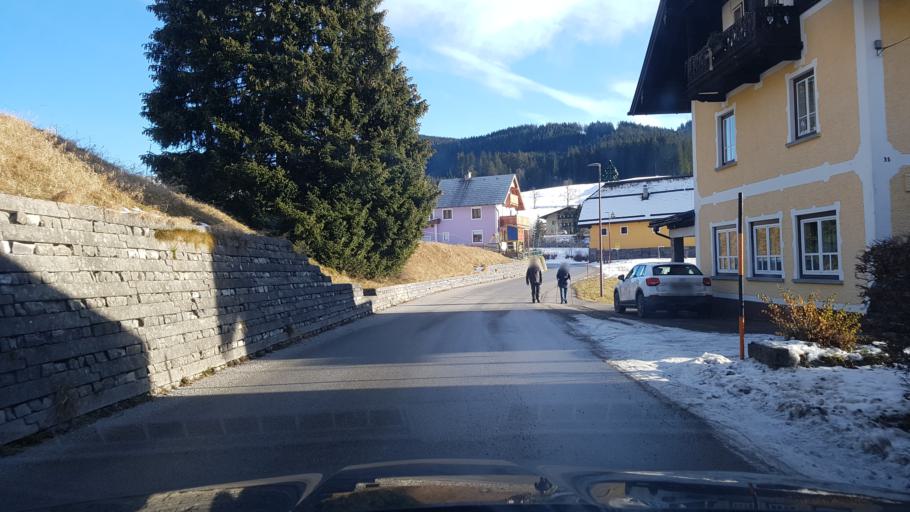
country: AT
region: Salzburg
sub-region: Politischer Bezirk Salzburg-Umgebung
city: Strobl
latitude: 47.5927
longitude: 13.4682
